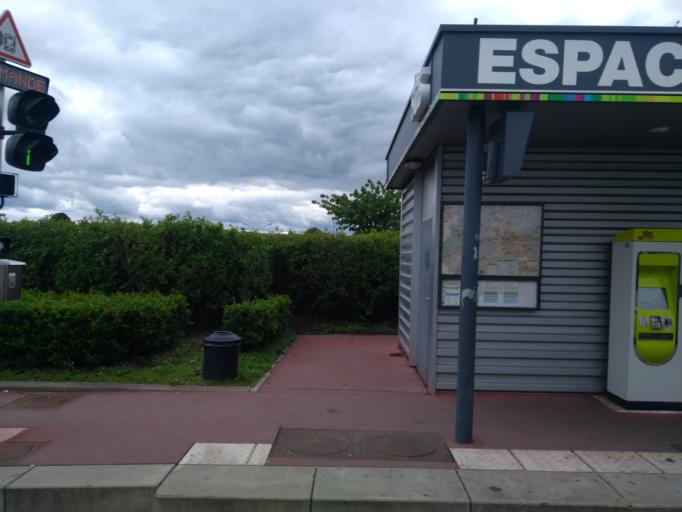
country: FR
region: Rhone-Alpes
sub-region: Departement de la Loire
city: Villars
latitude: 45.4769
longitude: 4.3645
